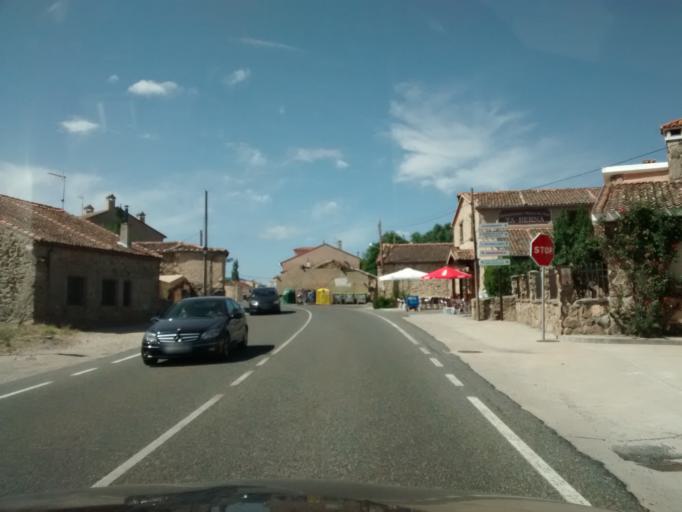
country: ES
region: Castille and Leon
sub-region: Provincia de Segovia
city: Collado Hermoso
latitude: 41.0399
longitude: -3.9172
